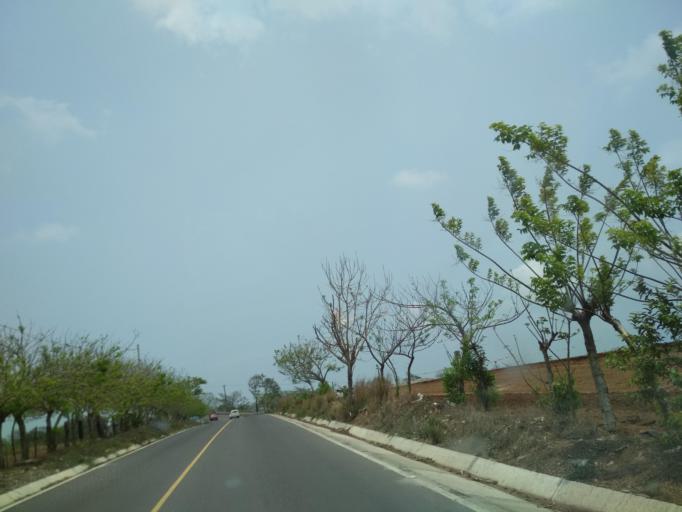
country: MX
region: Veracruz
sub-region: Veracruz
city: Delfino Victoria (Santa Fe)
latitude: 19.1737
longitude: -96.2712
